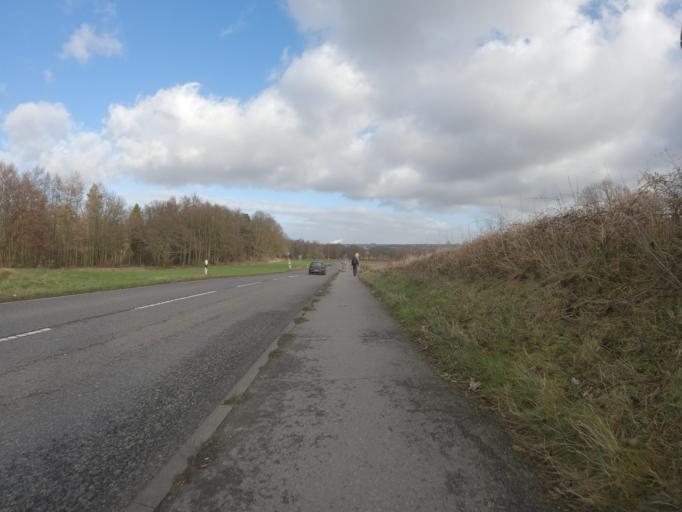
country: DE
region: North Rhine-Westphalia
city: Stolberg
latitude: 50.7763
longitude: 6.1885
